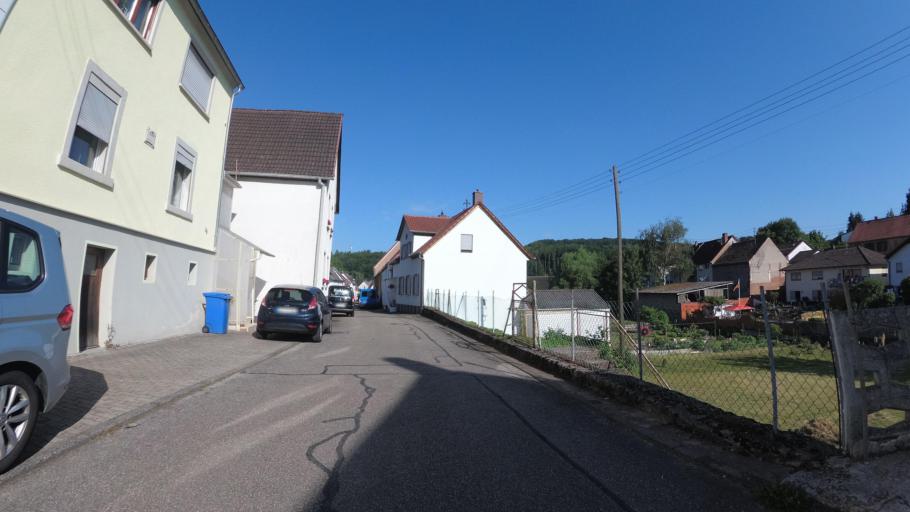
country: DE
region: Rheinland-Pfalz
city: Althornbach
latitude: 49.2150
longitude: 7.3377
